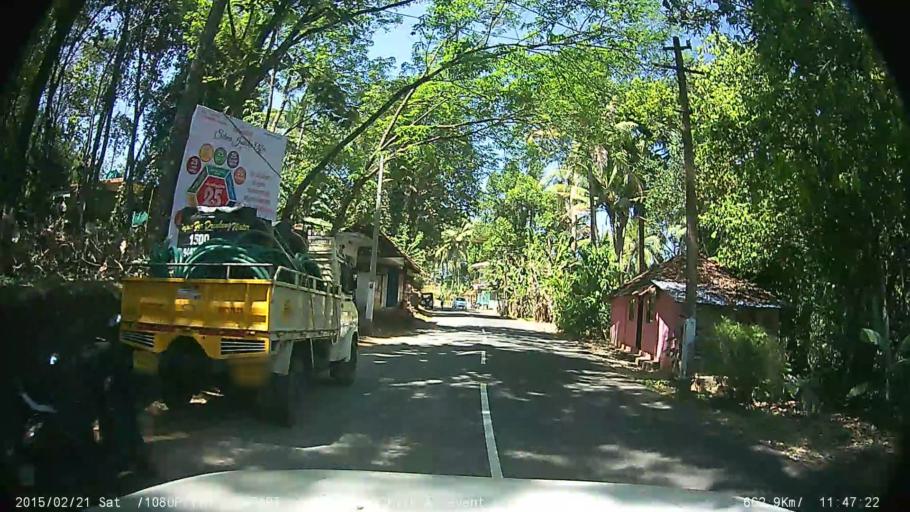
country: IN
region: Kerala
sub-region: Kottayam
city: Lalam
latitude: 9.7749
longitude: 76.7162
